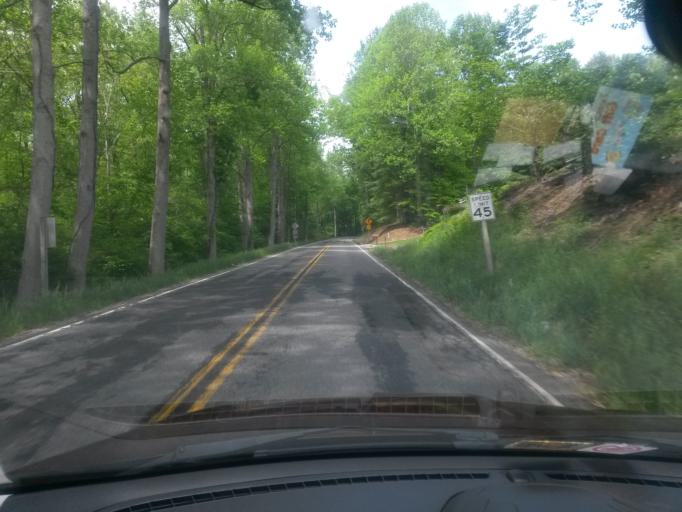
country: US
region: Virginia
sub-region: Floyd County
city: Floyd
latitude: 36.8953
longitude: -80.3229
